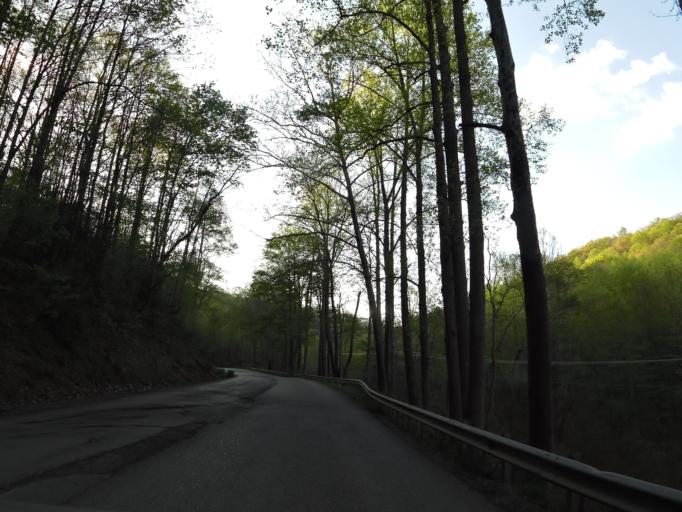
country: US
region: Kentucky
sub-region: Bell County
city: Middlesboro
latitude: 36.6148
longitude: -83.8346
